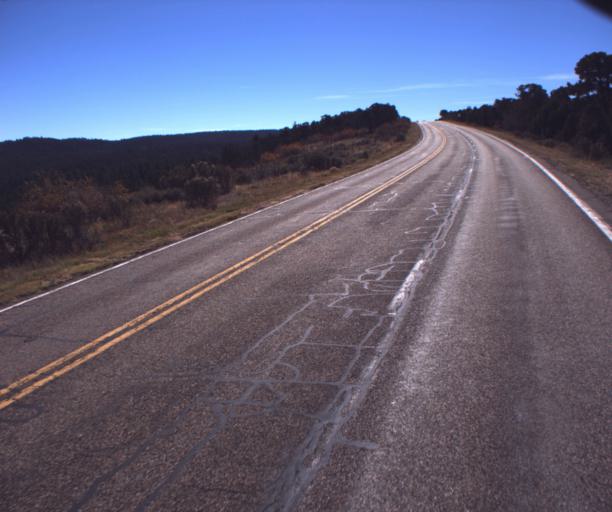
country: US
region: Arizona
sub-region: Coconino County
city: Fredonia
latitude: 36.8064
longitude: -112.2555
